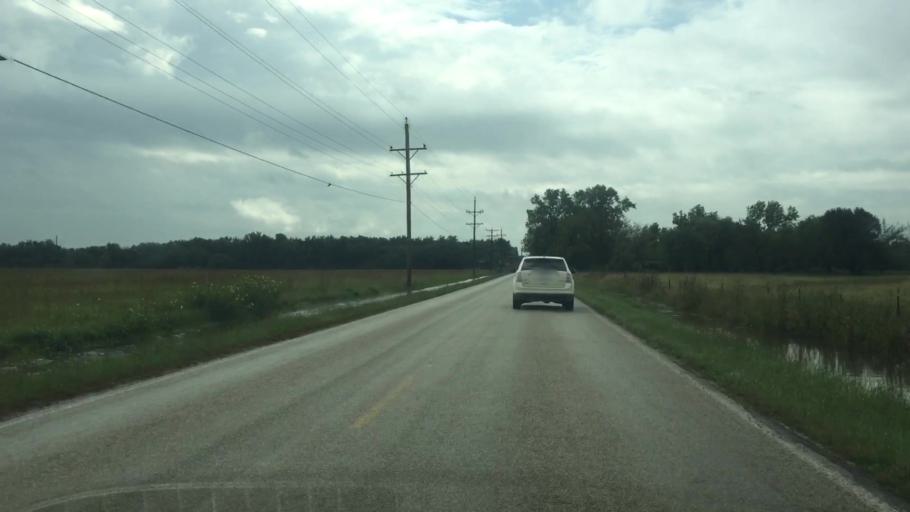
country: US
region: Kansas
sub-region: Allen County
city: Humboldt
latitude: 37.8729
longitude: -95.4369
